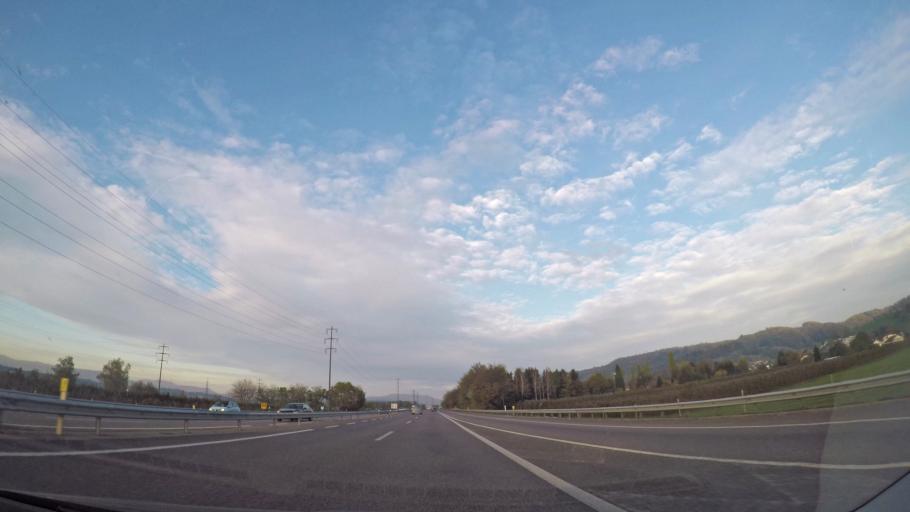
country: CH
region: Aargau
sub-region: Bezirk Aarau
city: Muhen
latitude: 47.3391
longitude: 8.0421
